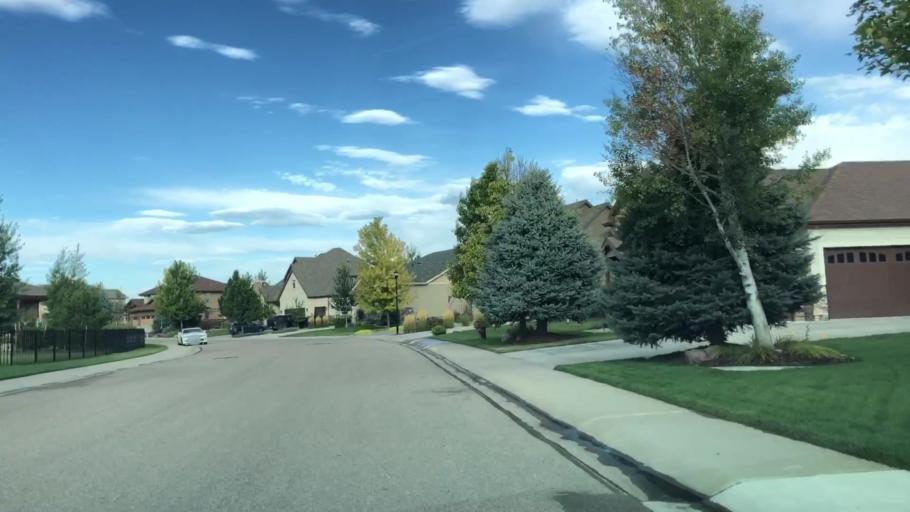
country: US
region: Colorado
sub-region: Weld County
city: Windsor
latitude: 40.4481
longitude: -104.9728
